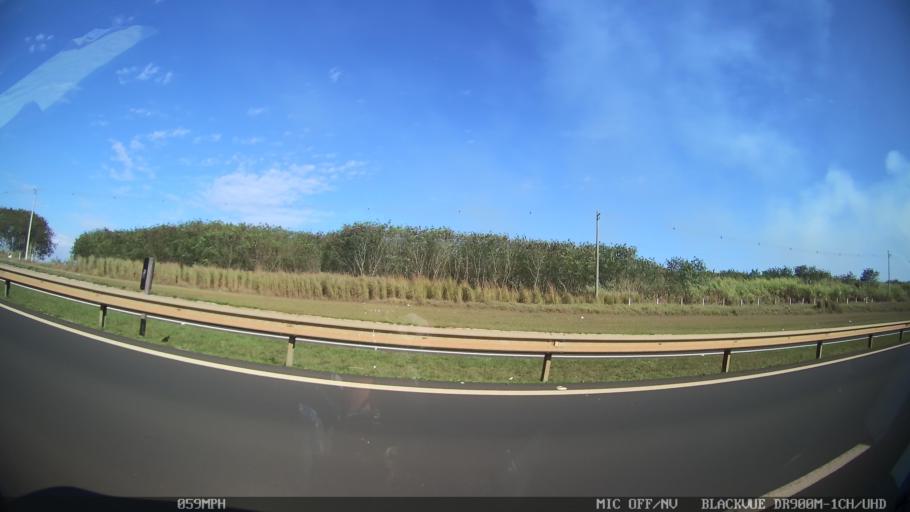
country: BR
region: Sao Paulo
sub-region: Piracicaba
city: Piracicaba
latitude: -22.6817
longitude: -47.5701
